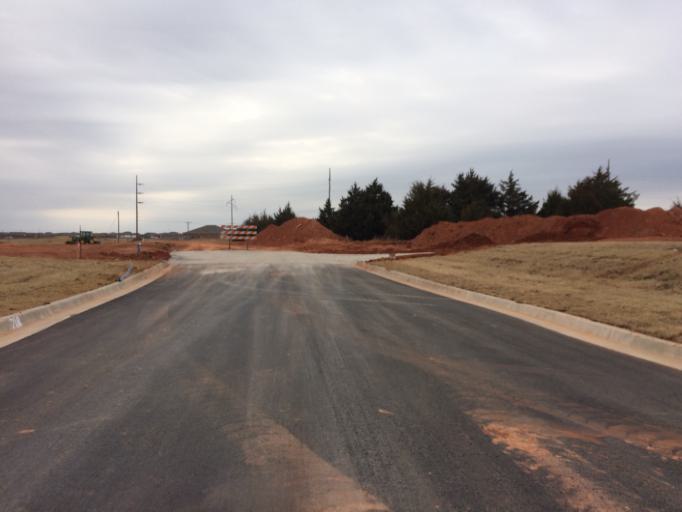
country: US
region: Oklahoma
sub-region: Cleveland County
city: Norman
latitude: 35.2562
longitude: -97.4558
